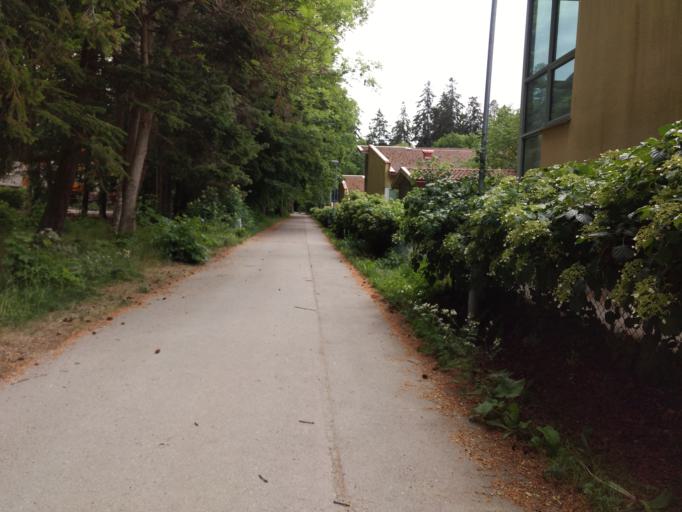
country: SE
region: Stockholm
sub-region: Upplands Vasby Kommun
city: Upplands Vaesby
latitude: 59.5290
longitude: 17.9095
